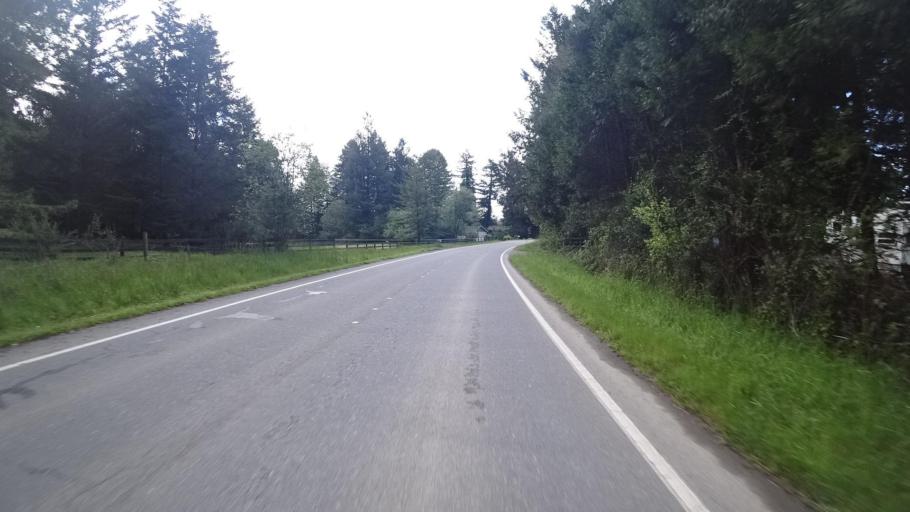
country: US
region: California
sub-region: Humboldt County
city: McKinleyville
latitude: 40.9692
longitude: -124.0364
